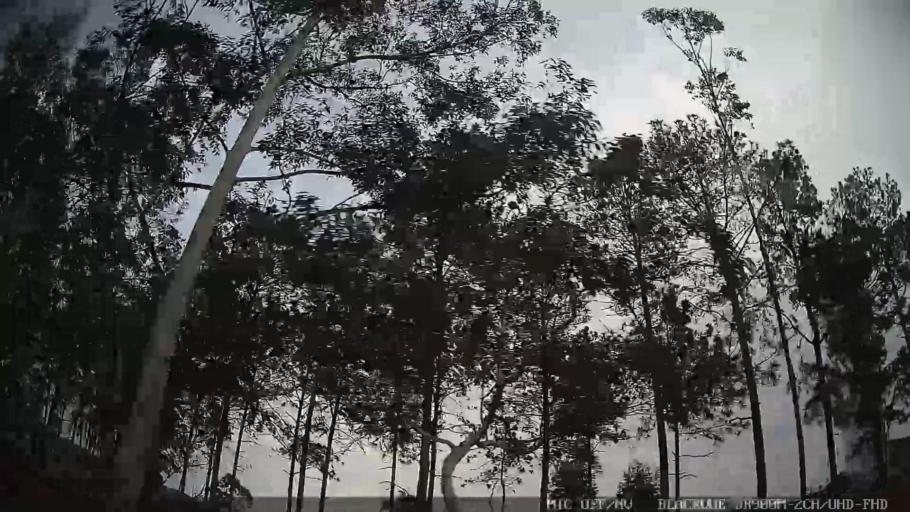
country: BR
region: Sao Paulo
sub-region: Itatiba
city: Itatiba
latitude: -23.0020
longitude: -46.8602
